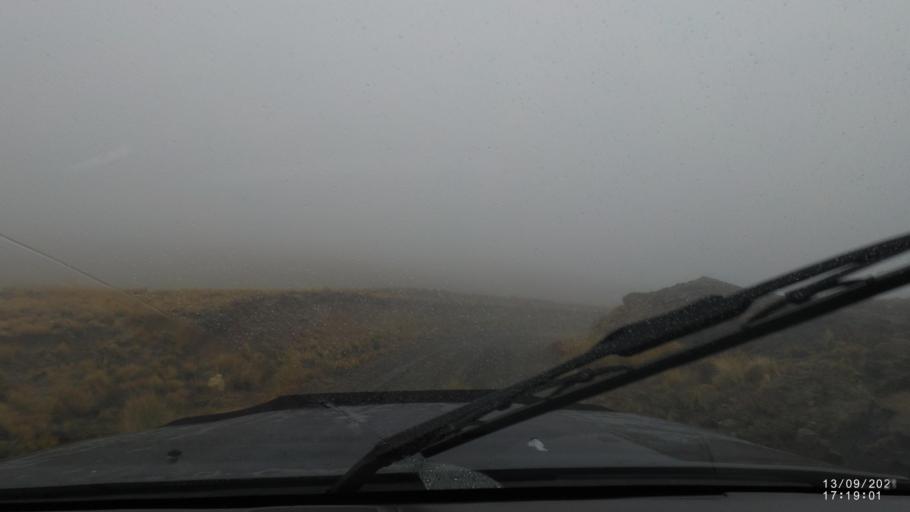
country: BO
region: Cochabamba
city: Colomi
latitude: -17.3515
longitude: -65.7619
